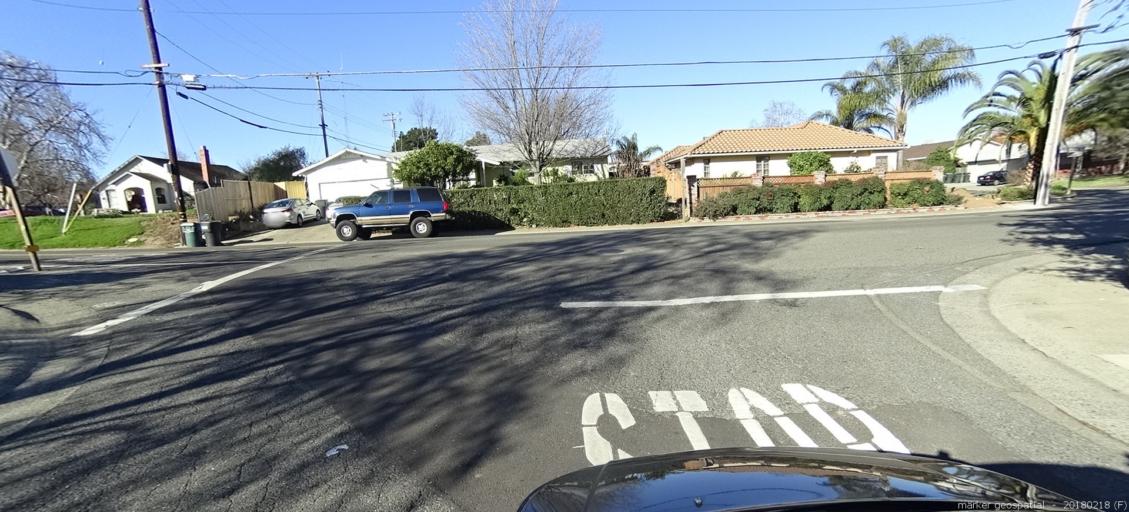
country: US
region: California
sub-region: Sacramento County
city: Orangevale
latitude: 38.6760
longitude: -121.2395
